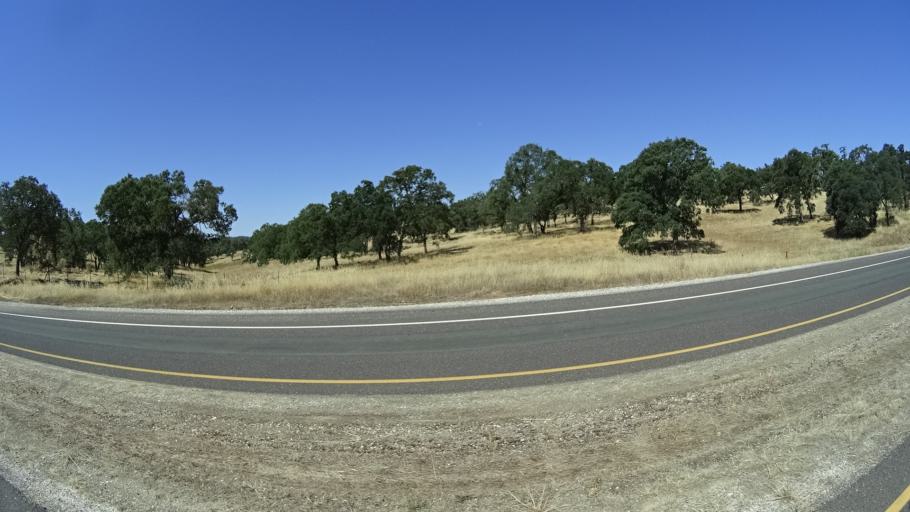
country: US
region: California
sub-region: Calaveras County
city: Copperopolis
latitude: 37.9648
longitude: -120.6555
